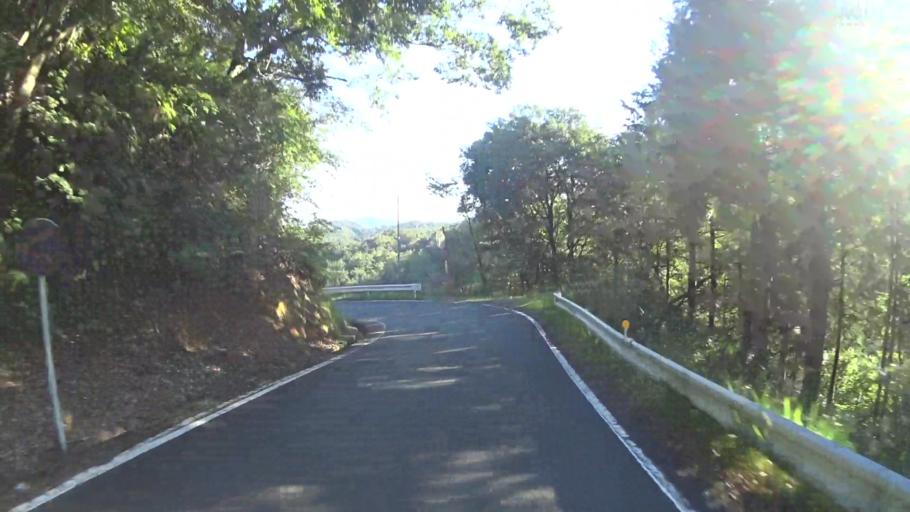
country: JP
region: Hyogo
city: Toyooka
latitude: 35.6141
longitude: 134.8757
